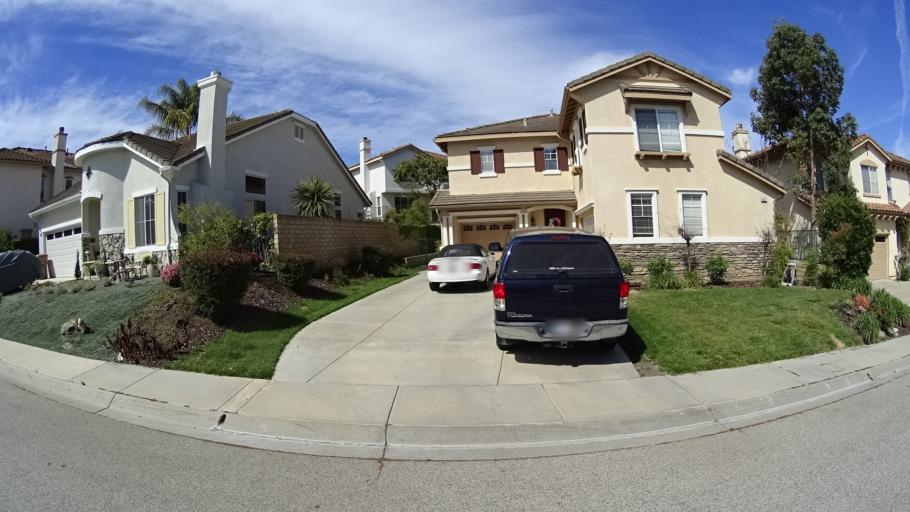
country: US
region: California
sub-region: Ventura County
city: Casa Conejo
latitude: 34.1710
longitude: -118.9728
